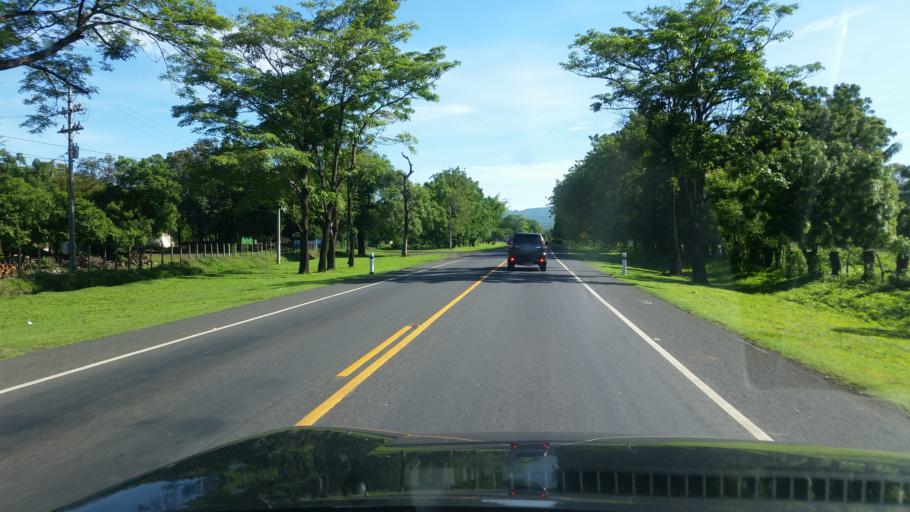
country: NI
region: Leon
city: Telica
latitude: 12.5064
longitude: -86.8601
